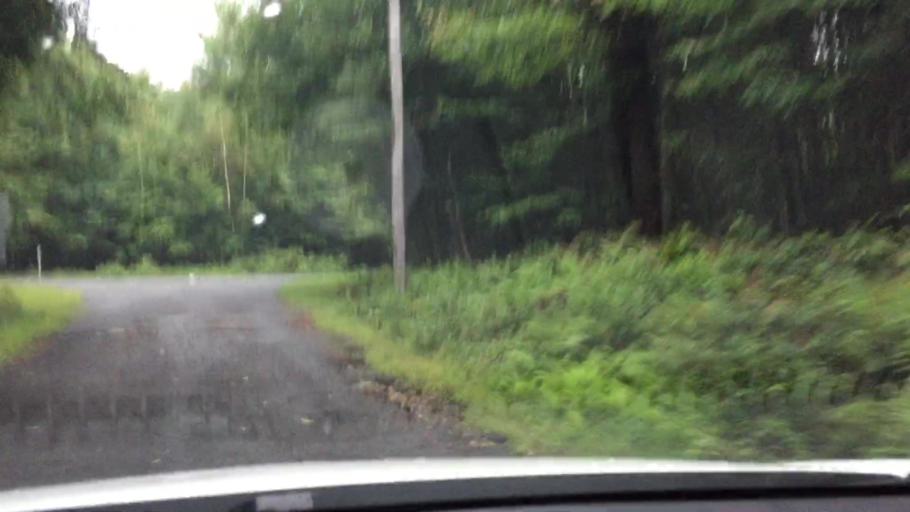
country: US
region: Massachusetts
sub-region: Berkshire County
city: Otis
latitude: 42.1453
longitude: -73.0494
